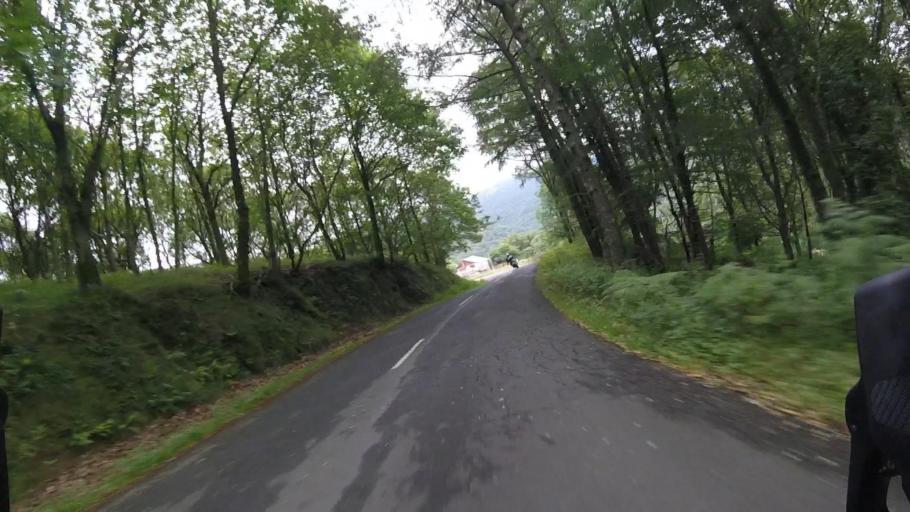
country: ES
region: Basque Country
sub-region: Provincia de Guipuzcoa
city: Irun
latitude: 43.2725
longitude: -1.8080
